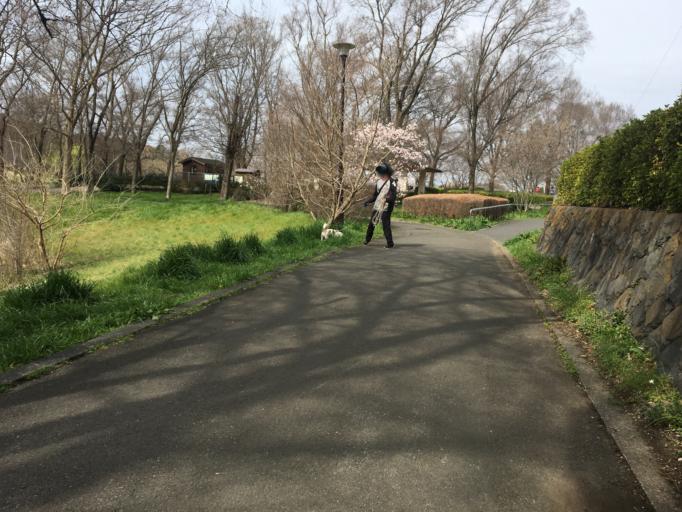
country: JP
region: Tokyo
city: Nishi-Tokyo-shi
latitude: 35.6922
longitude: 139.5186
